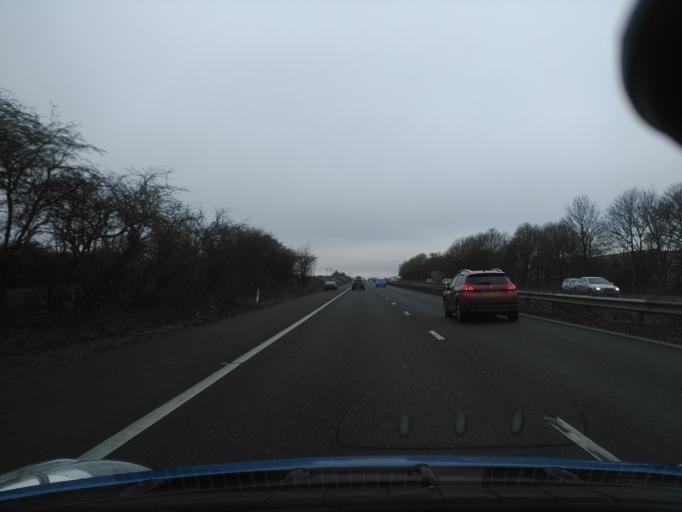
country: GB
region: England
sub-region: Hertfordshire
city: Stevenage
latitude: 51.9007
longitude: -0.2204
